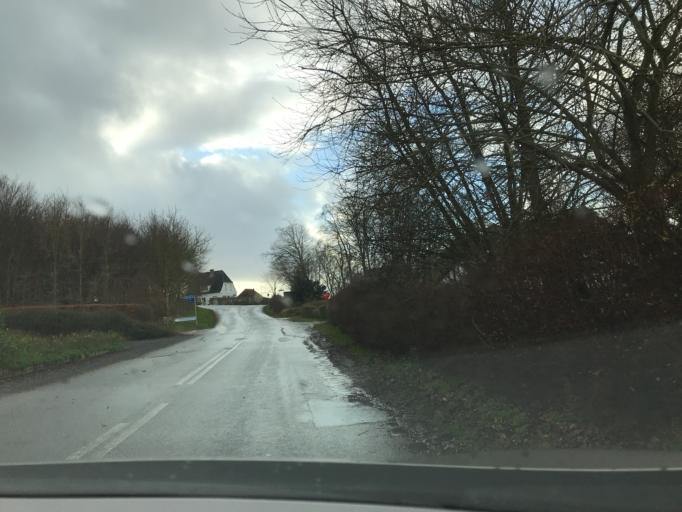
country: DK
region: South Denmark
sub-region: Assens Kommune
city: Arup
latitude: 55.3322
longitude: 9.9713
